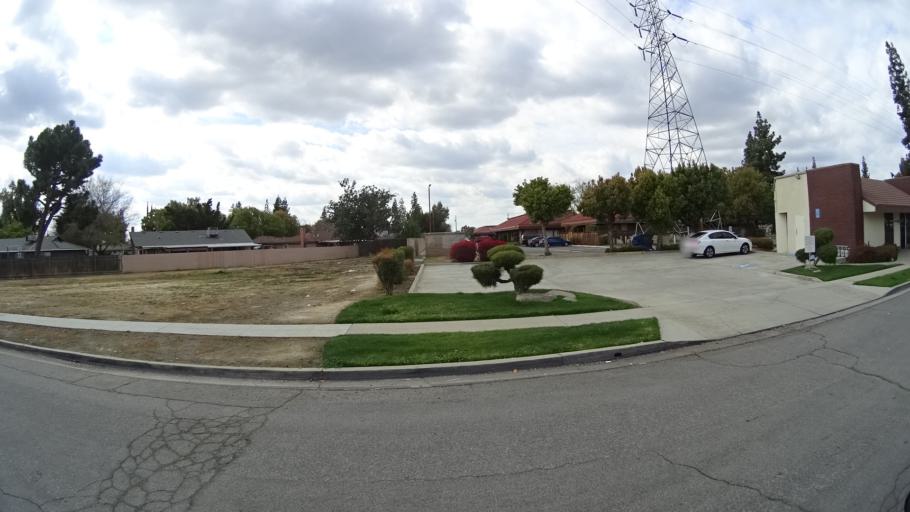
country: US
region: California
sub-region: Fresno County
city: Clovis
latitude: 36.8357
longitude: -119.7696
